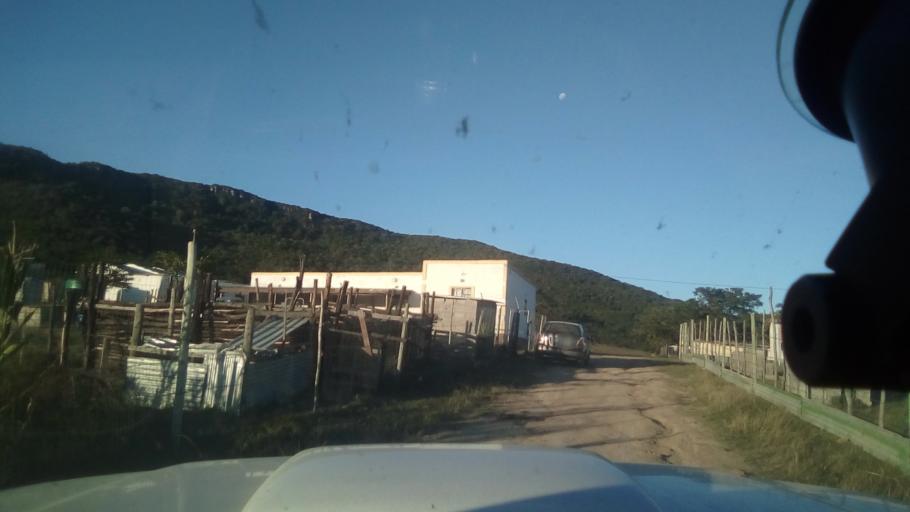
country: ZA
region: Eastern Cape
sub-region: Buffalo City Metropolitan Municipality
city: Bhisho
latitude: -32.7353
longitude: 27.3777
